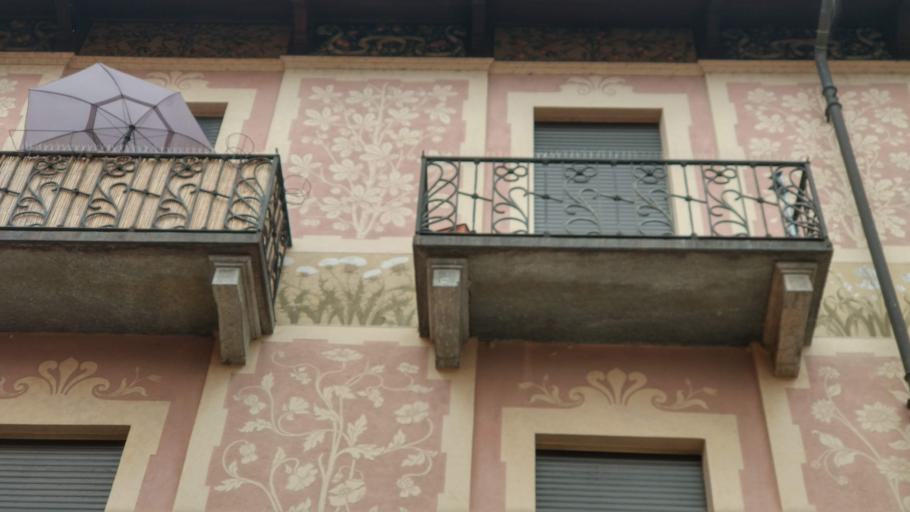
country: IT
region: Piedmont
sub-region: Provincia di Cuneo
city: Canale
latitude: 44.7971
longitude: 7.9897
